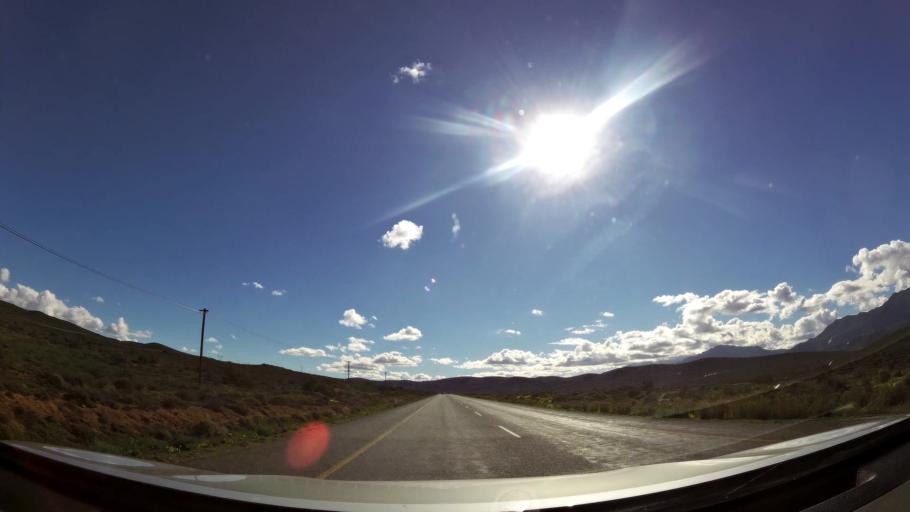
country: ZA
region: Western Cape
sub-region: Cape Winelands District Municipality
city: Worcester
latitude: -33.7467
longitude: 19.7024
